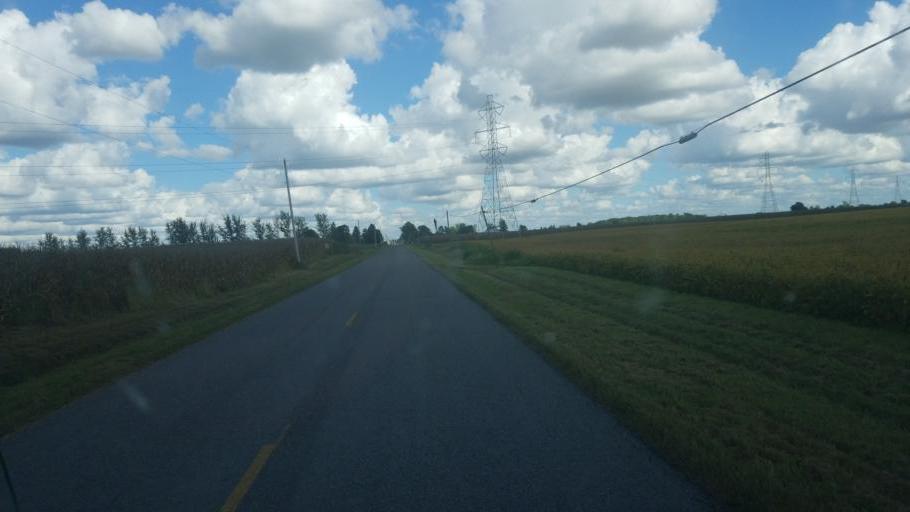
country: US
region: Ohio
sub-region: Logan County
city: Northwood
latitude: 40.5037
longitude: -83.6016
